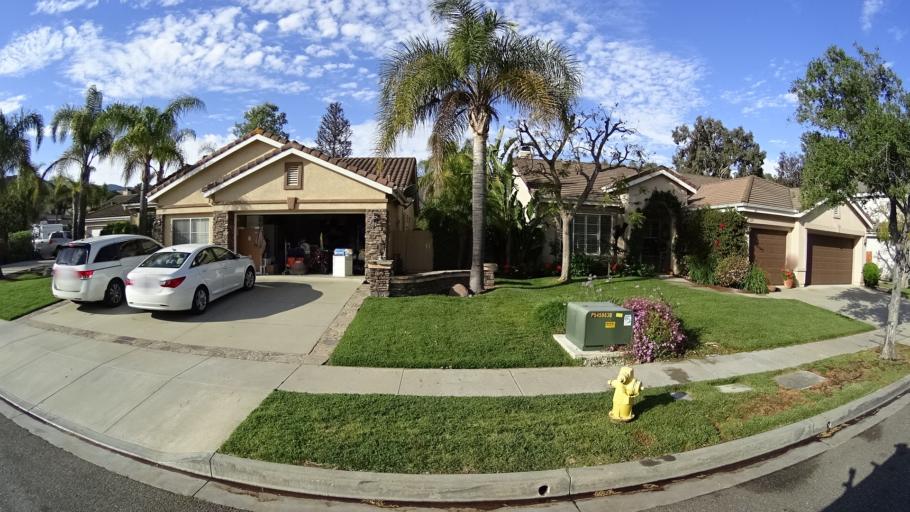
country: US
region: California
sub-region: Ventura County
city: Casa Conejo
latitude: 34.1745
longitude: -118.9475
